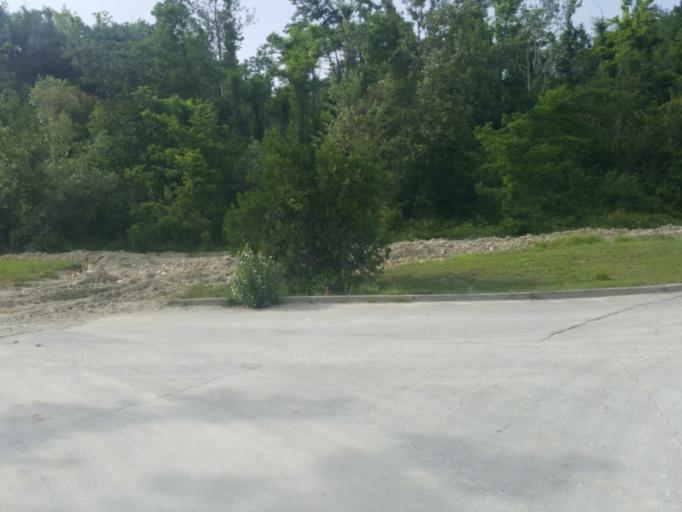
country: IT
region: Emilia-Romagna
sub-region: Provincia di Piacenza
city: Ponte dell'Olio
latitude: 44.8710
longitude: 9.6137
